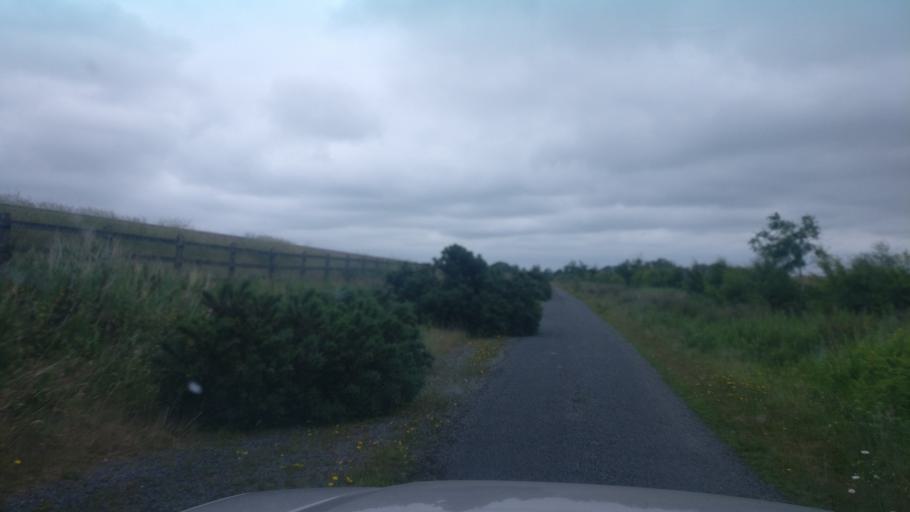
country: IE
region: Connaught
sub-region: County Galway
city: Ballinasloe
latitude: 53.2935
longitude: -8.3555
